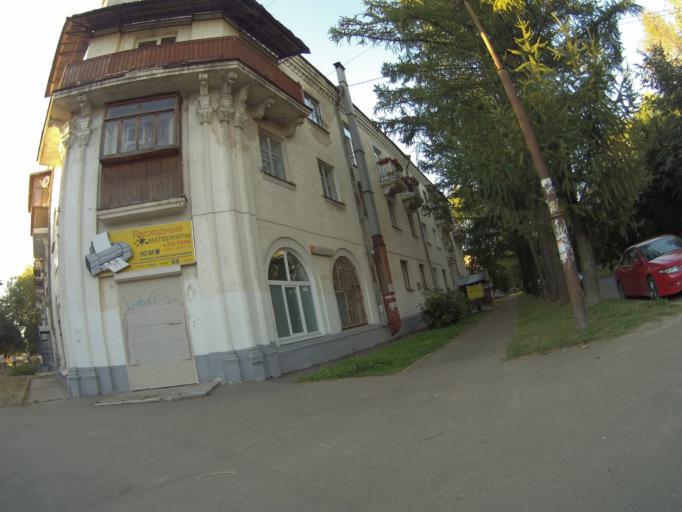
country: RU
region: Vladimir
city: Vladimir
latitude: 56.1454
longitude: 40.3837
